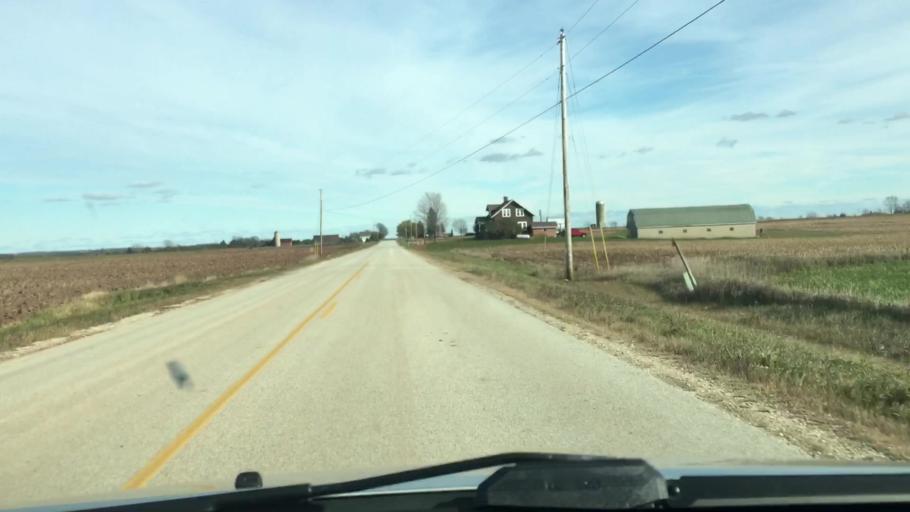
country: US
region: Wisconsin
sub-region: Kewaunee County
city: Algoma
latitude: 44.6974
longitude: -87.5956
